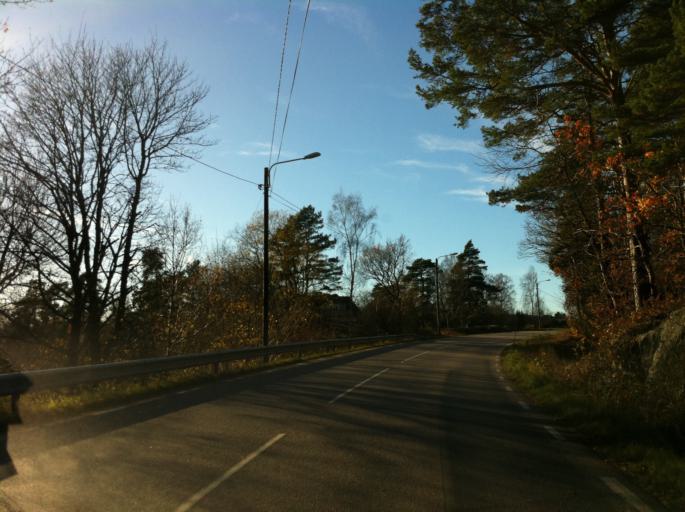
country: SE
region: Blekinge
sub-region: Karlshamns Kommun
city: Karlshamn
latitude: 56.1981
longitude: 14.9576
